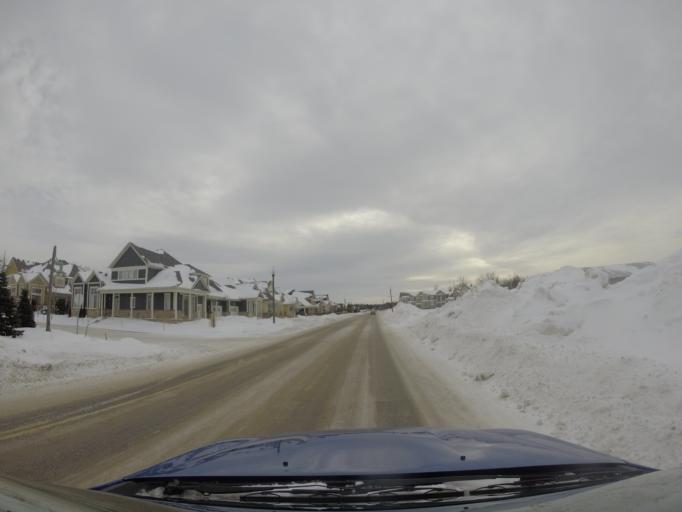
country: CA
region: Ontario
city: Wasaga Beach
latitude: 44.5288
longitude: -80.0082
